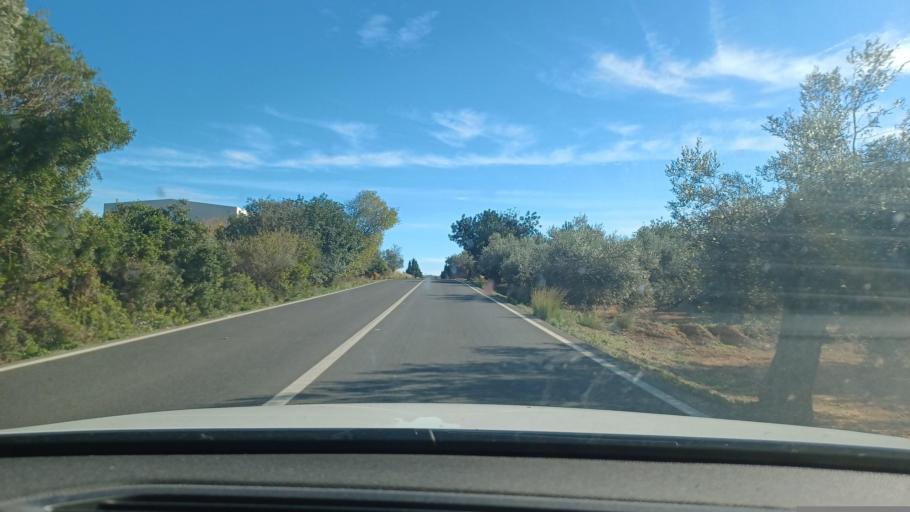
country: ES
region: Catalonia
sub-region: Provincia de Tarragona
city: Masdenverge
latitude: 40.7109
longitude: 0.5365
